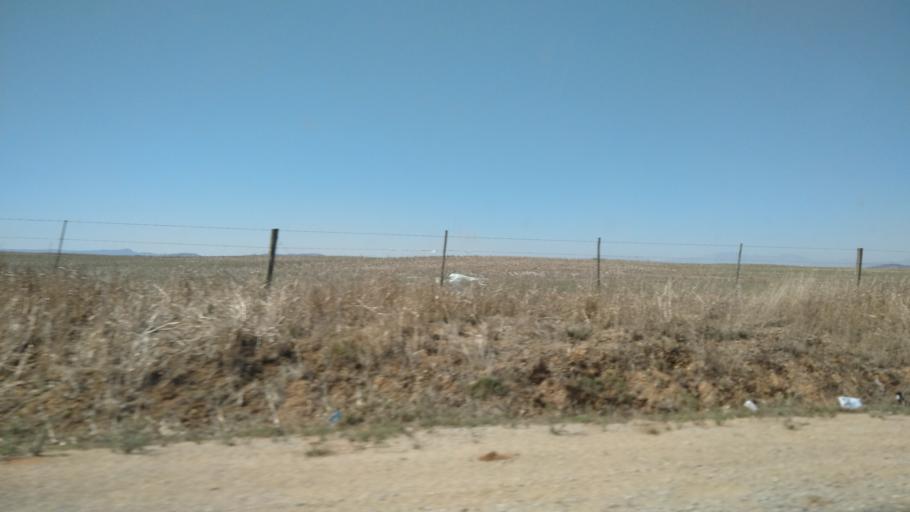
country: ZA
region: Western Cape
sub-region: West Coast District Municipality
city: Moorreesburg
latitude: -33.1809
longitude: 18.4932
